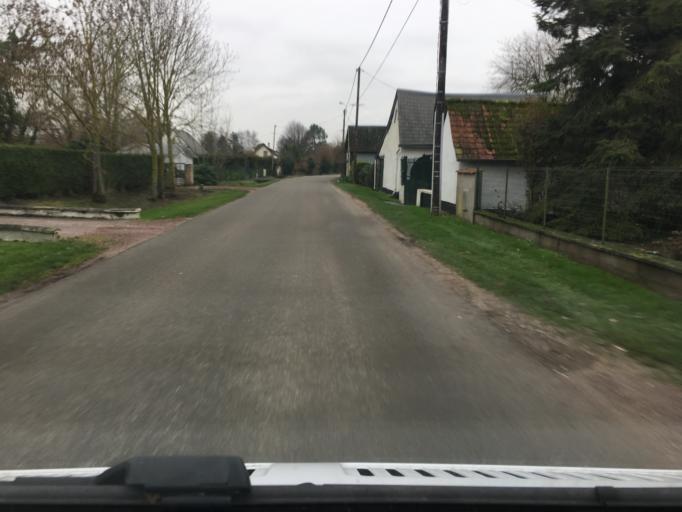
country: FR
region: Picardie
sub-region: Departement de la Somme
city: Pende
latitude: 50.1646
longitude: 1.5545
